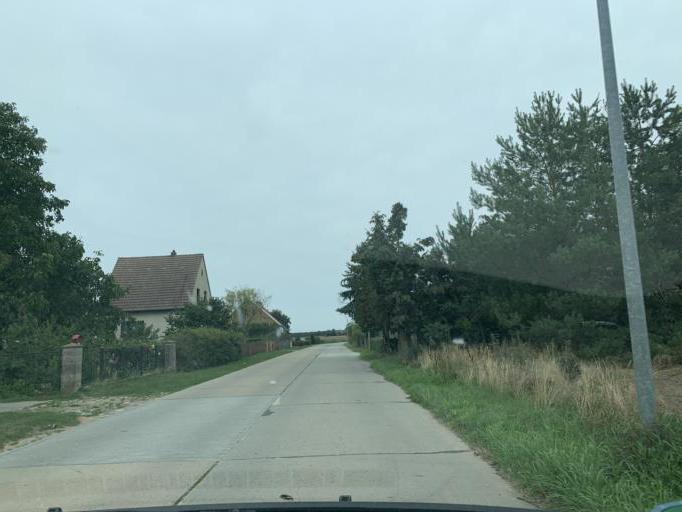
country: DE
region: Brandenburg
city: Zehdenick
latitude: 53.0078
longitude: 13.2752
